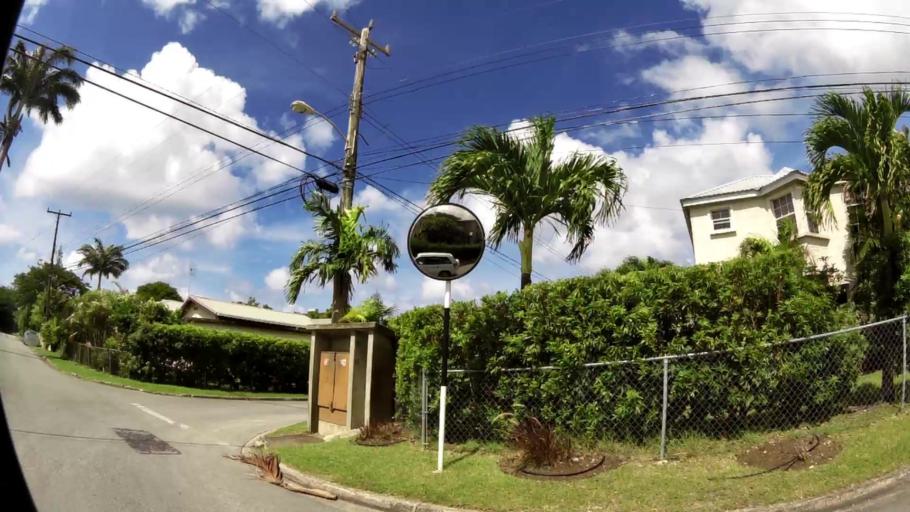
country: BB
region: Saint Michael
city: Bridgetown
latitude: 13.1408
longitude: -59.6241
